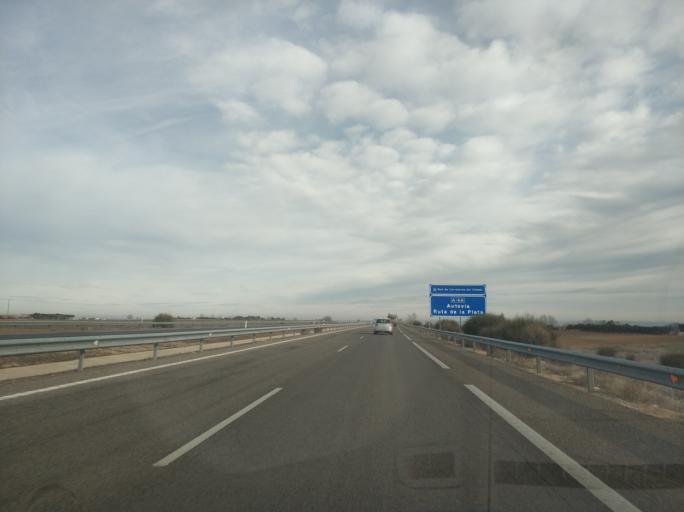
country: ES
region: Castille and Leon
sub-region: Provincia de Zamora
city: Morales del Vino
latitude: 41.4342
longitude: -5.7207
